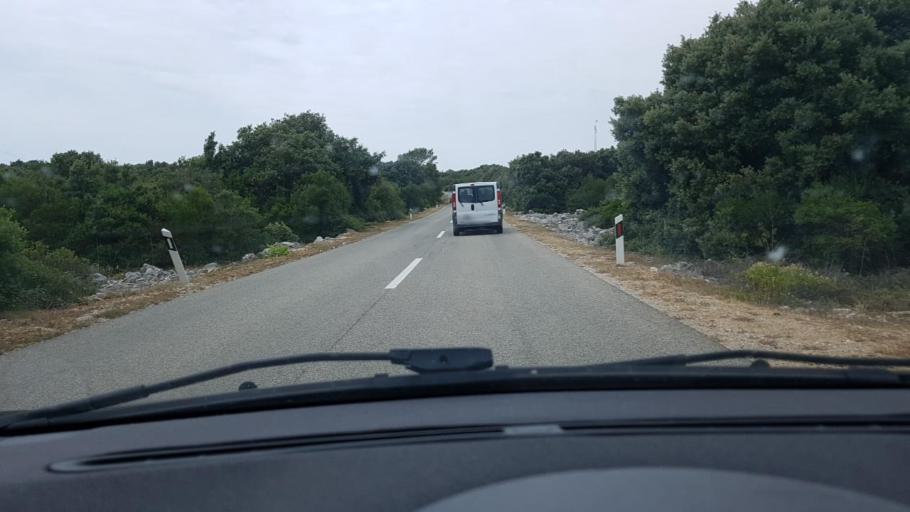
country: HR
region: Dubrovacko-Neretvanska
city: Smokvica
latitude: 42.9488
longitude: 16.9871
